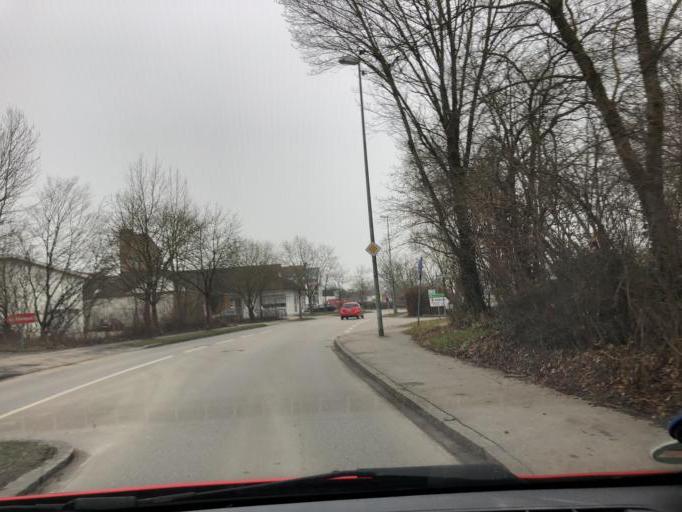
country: DE
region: Bavaria
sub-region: Upper Bavaria
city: Olching
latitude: 48.1986
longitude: 11.3332
